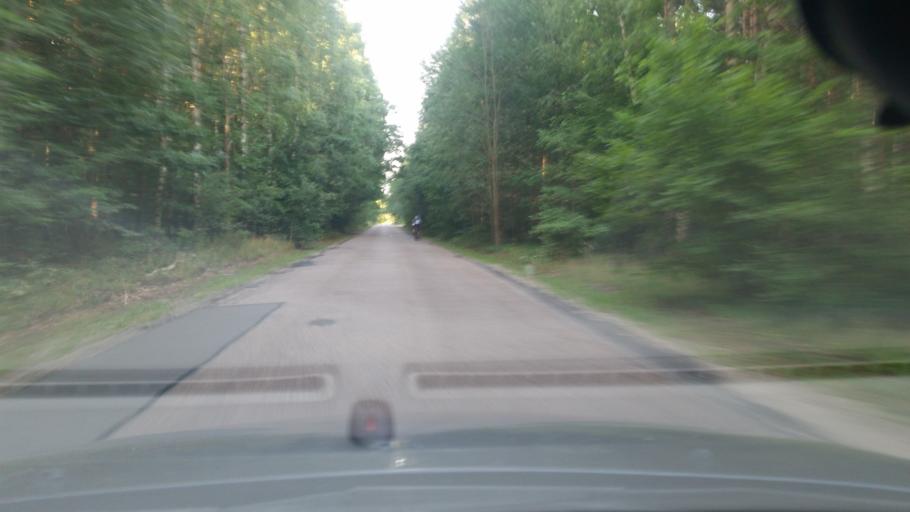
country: PL
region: Pomeranian Voivodeship
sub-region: Powiat wejherowski
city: Choczewo
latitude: 54.7609
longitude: 17.7721
